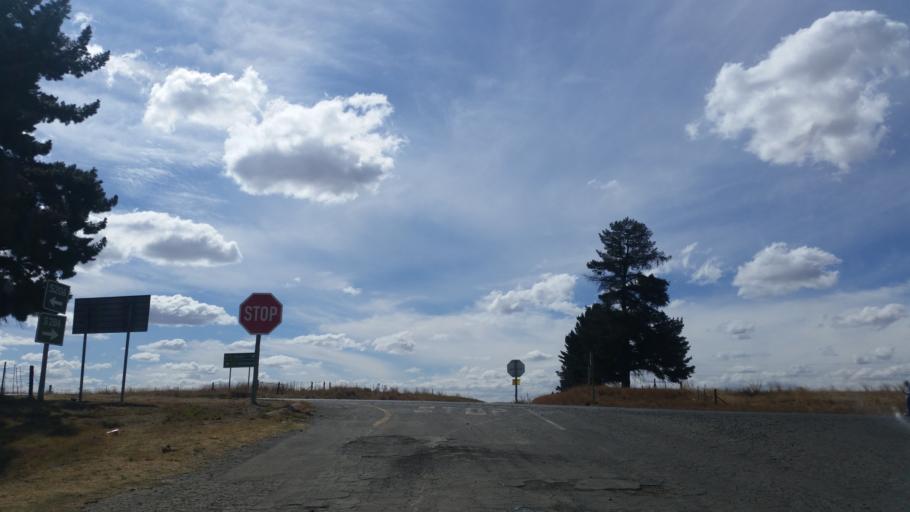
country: ZA
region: Orange Free State
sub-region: Thabo Mofutsanyana District Municipality
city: Bethlehem
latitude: -28.1392
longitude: 28.4858
